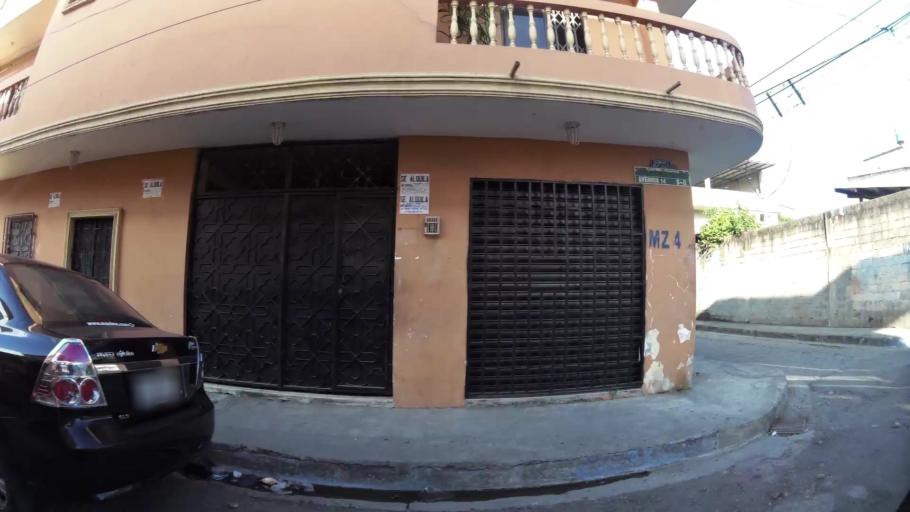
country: EC
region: Guayas
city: Guayaquil
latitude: -2.2256
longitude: -79.9093
